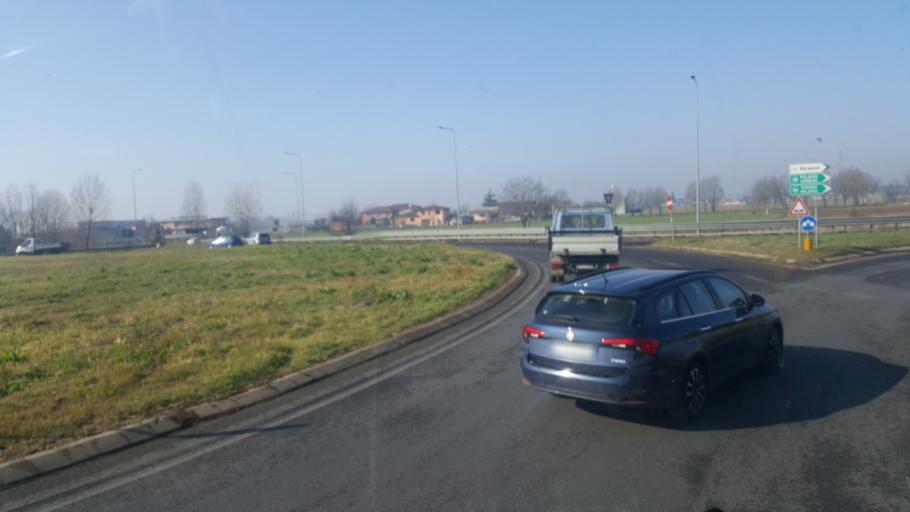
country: IT
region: Lombardy
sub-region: Citta metropolitana di Milano
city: Magenta
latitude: 45.4671
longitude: 8.8641
